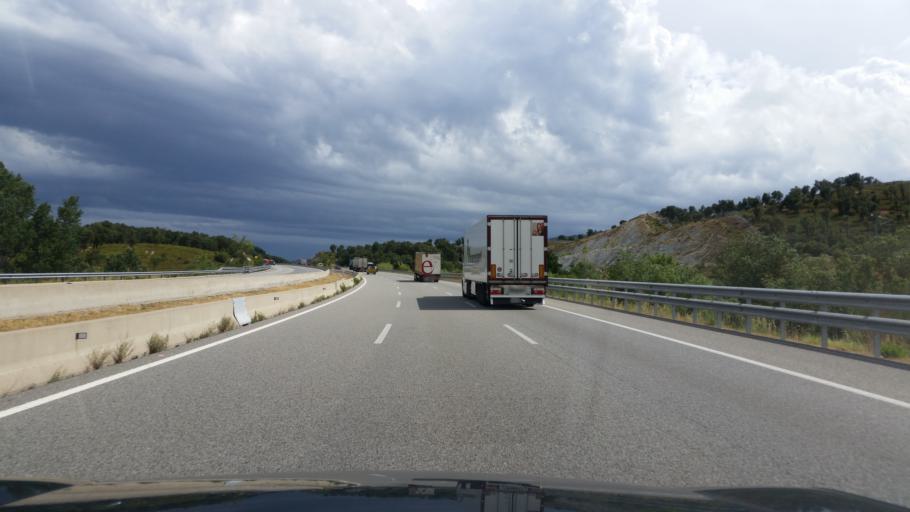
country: ES
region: Catalonia
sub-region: Provincia de Girona
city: Capmany
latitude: 42.3772
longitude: 2.8864
